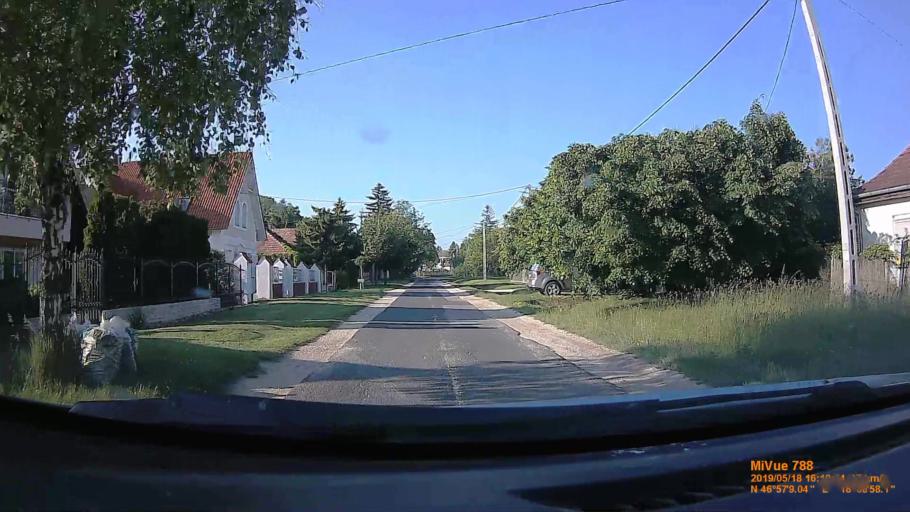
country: HU
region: Somogy
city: Balatonszabadi
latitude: 46.9526
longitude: 18.1495
